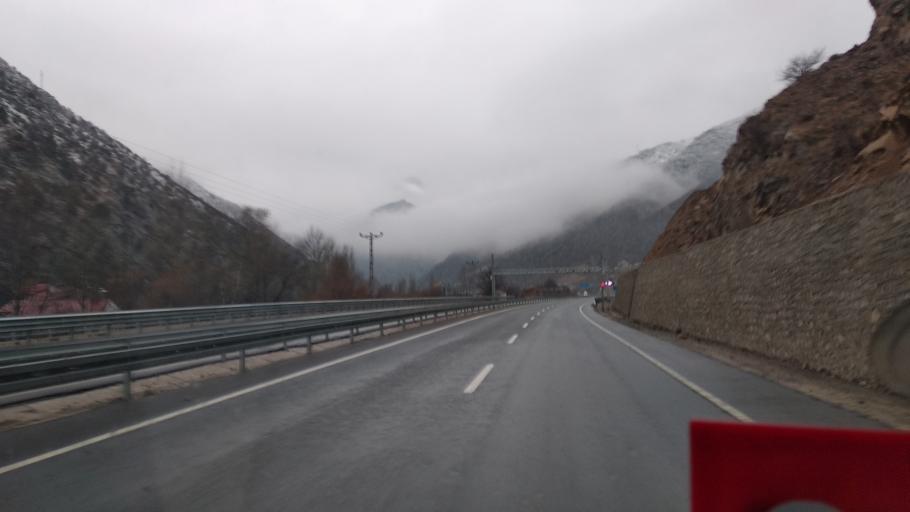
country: TR
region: Gumushane
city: Torul
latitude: 40.5464
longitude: 39.3218
